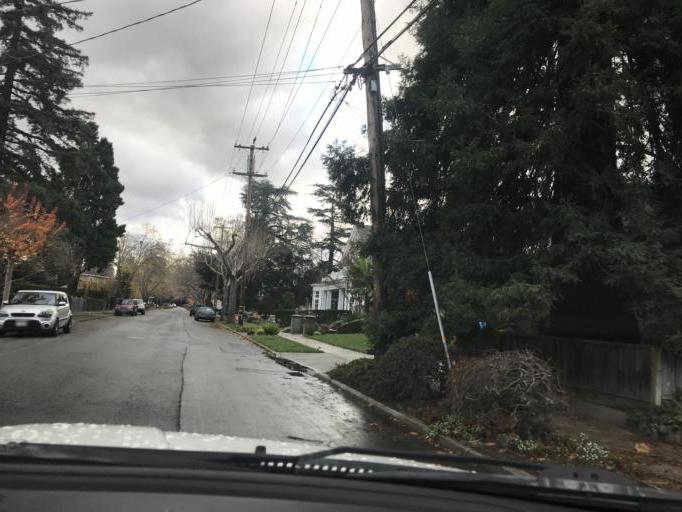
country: US
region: California
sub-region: Santa Clara County
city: Buena Vista
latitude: 37.2986
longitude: -121.9020
